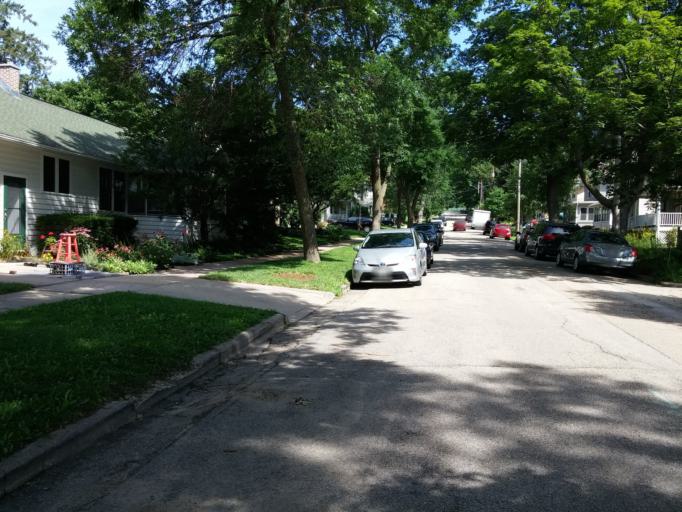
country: US
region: Wisconsin
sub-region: Dane County
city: Shorewood Hills
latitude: 43.0585
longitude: -89.4284
